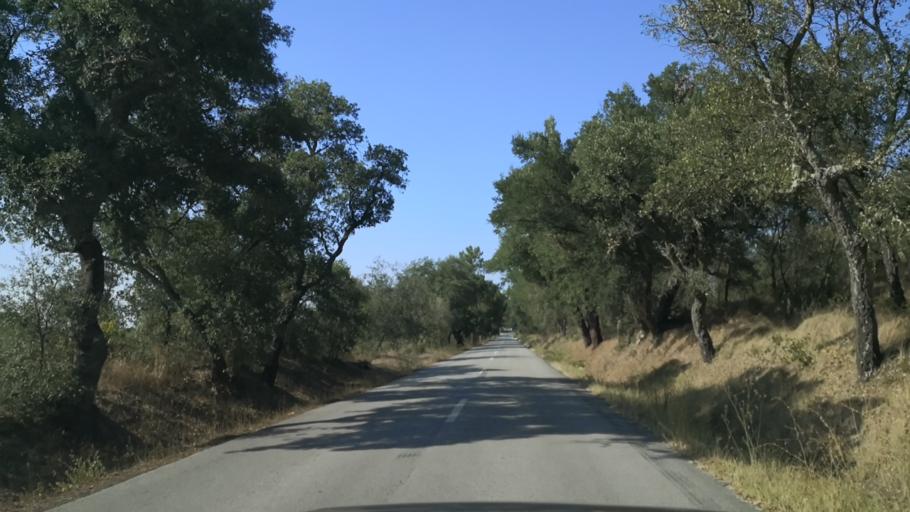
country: PT
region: Santarem
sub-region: Benavente
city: Poceirao
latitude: 38.7569
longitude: -8.6325
